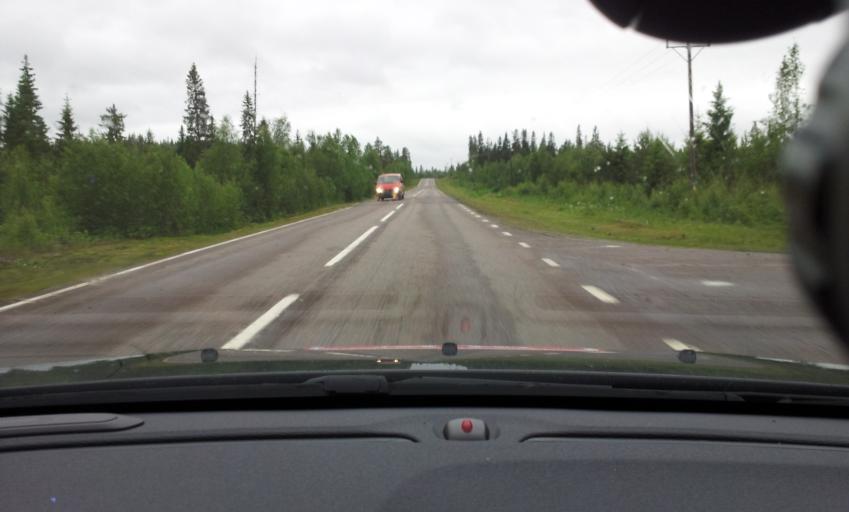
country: SE
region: Jaemtland
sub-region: Ragunda Kommun
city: Hammarstrand
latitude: 63.2093
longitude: 15.9507
